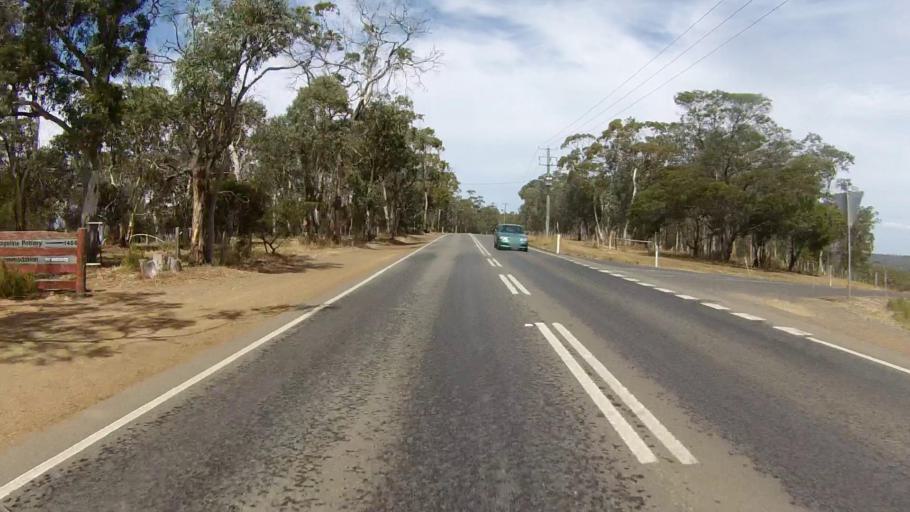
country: AU
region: Tasmania
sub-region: Clarence
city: Sandford
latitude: -42.9721
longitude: 147.5036
